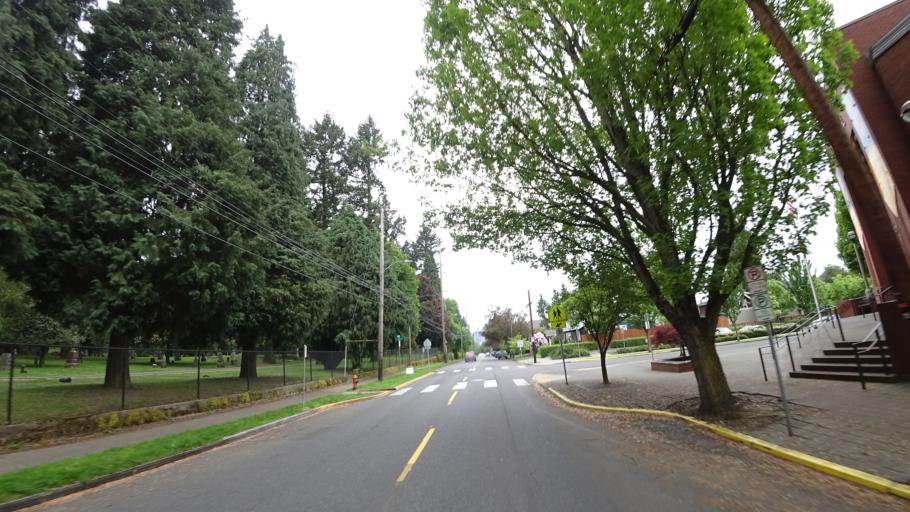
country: US
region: Oregon
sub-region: Multnomah County
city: Portland
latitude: 45.5193
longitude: -122.6411
